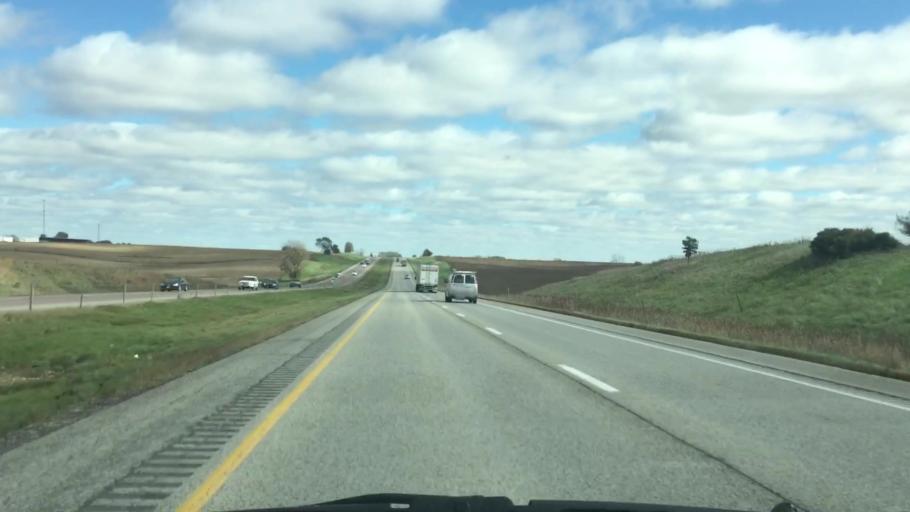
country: US
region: Iowa
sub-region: Iowa County
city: Marengo
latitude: 41.6959
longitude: -92.1990
